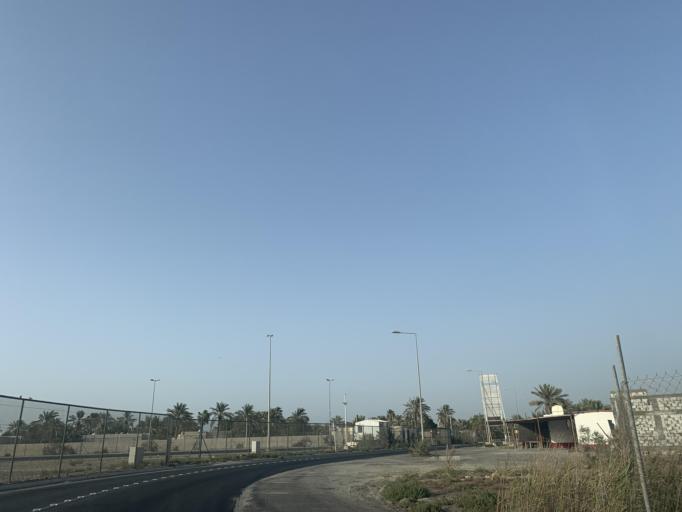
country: BH
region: Central Governorate
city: Madinat Hamad
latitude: 26.1745
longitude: 50.4527
